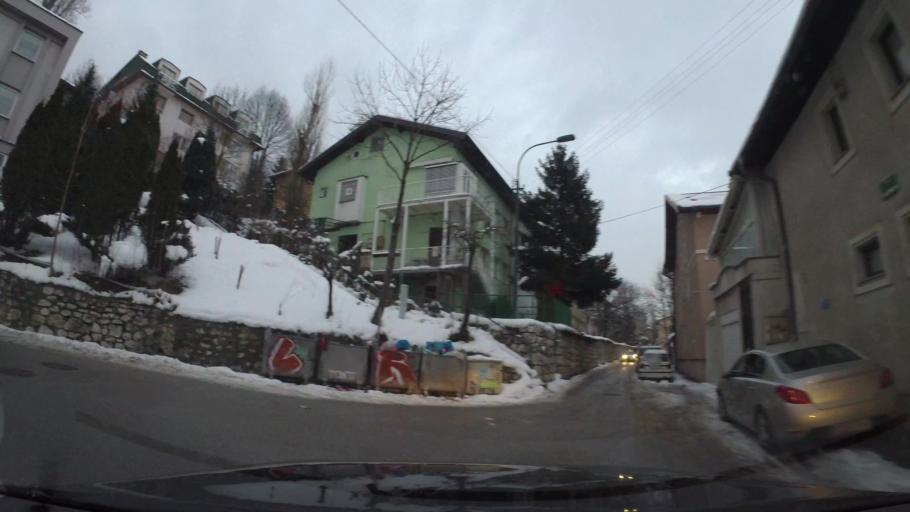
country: BA
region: Federation of Bosnia and Herzegovina
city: Kobilja Glava
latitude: 43.8597
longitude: 18.4040
